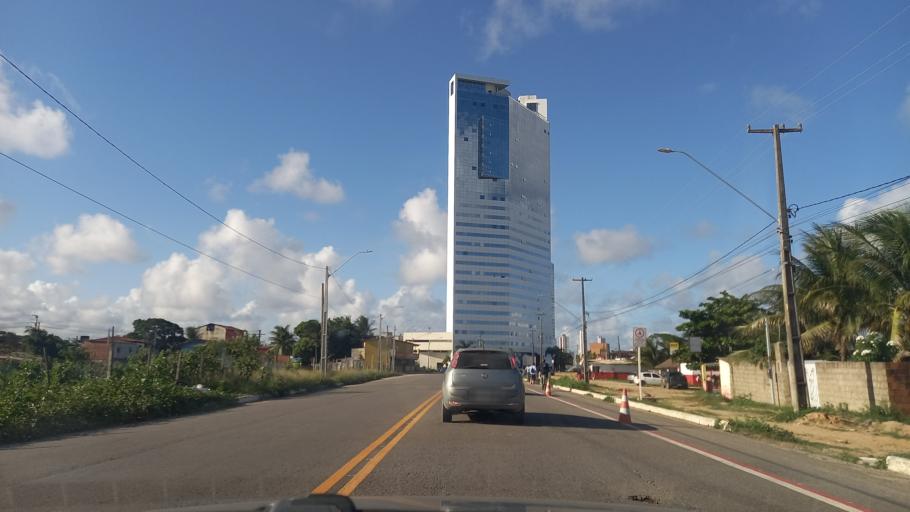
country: BR
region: Pernambuco
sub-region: Jaboatao Dos Guararapes
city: Jaboatao
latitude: -8.2275
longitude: -34.9324
